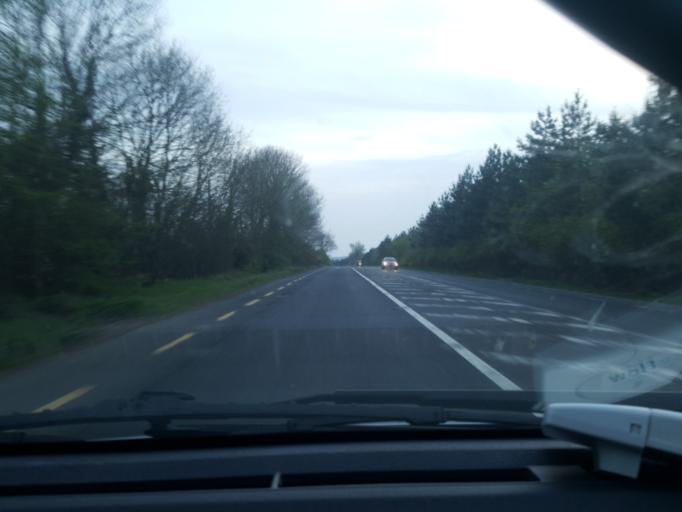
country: IE
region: Munster
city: Cahir
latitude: 52.3654
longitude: -7.9697
